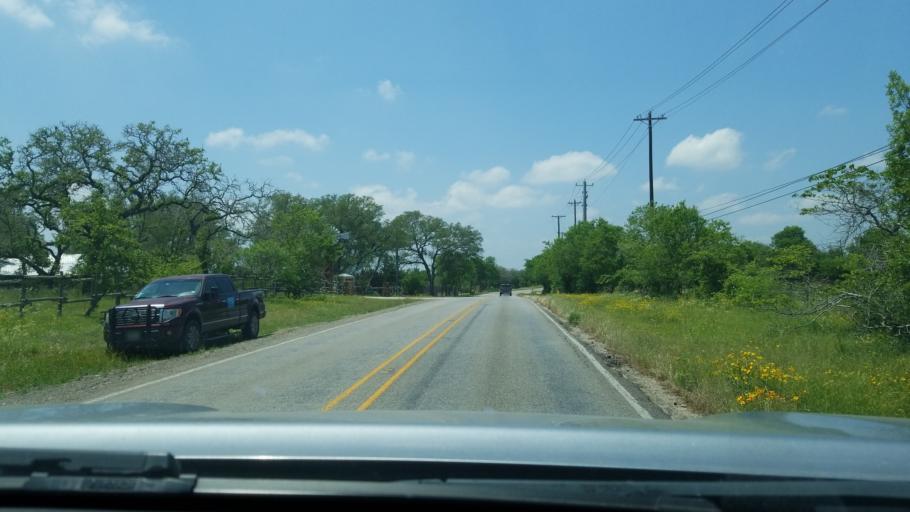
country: US
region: Texas
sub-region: Hays County
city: Woodcreek
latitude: 30.0335
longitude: -98.1758
